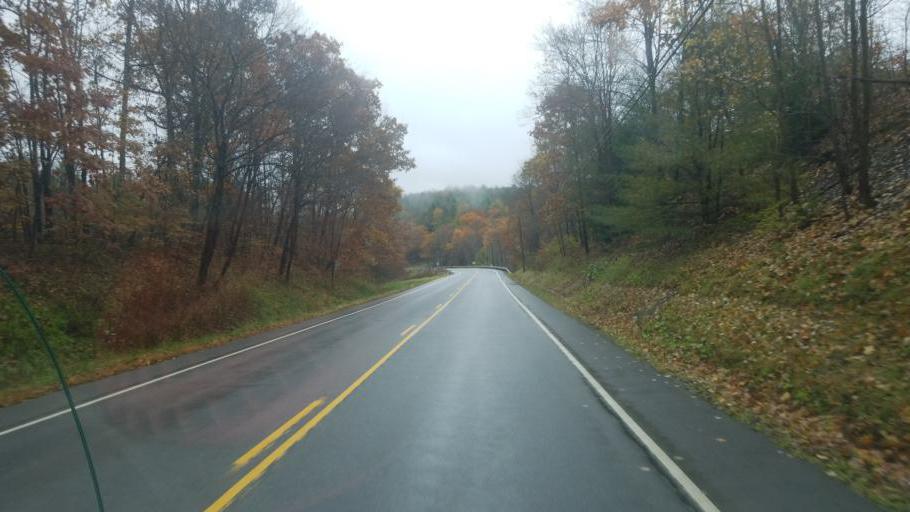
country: US
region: Pennsylvania
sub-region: Clearfield County
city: Shiloh
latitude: 41.1082
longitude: -78.1598
